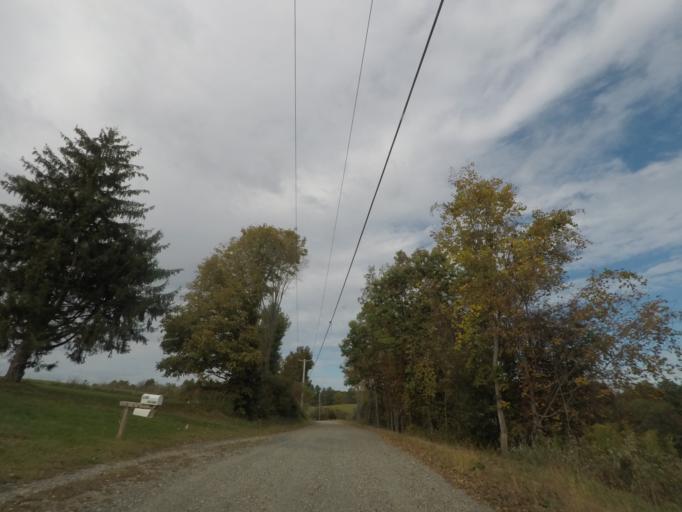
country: US
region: New York
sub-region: Rensselaer County
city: Nassau
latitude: 42.5784
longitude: -73.6134
